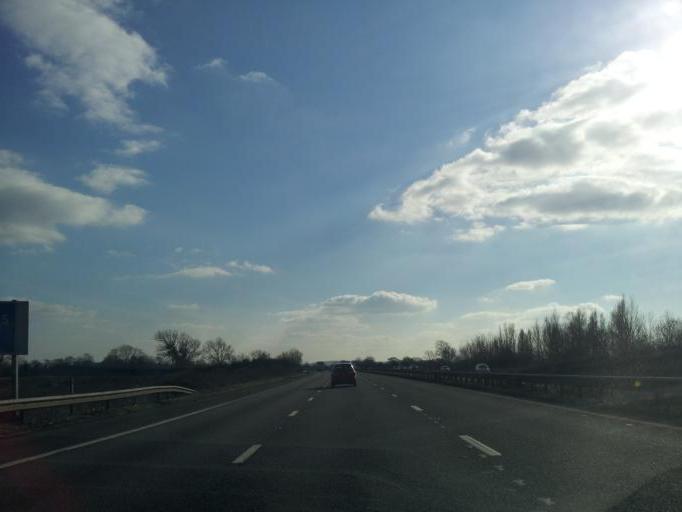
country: GB
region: England
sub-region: North Somerset
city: Kenn
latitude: 51.4183
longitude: -2.8490
